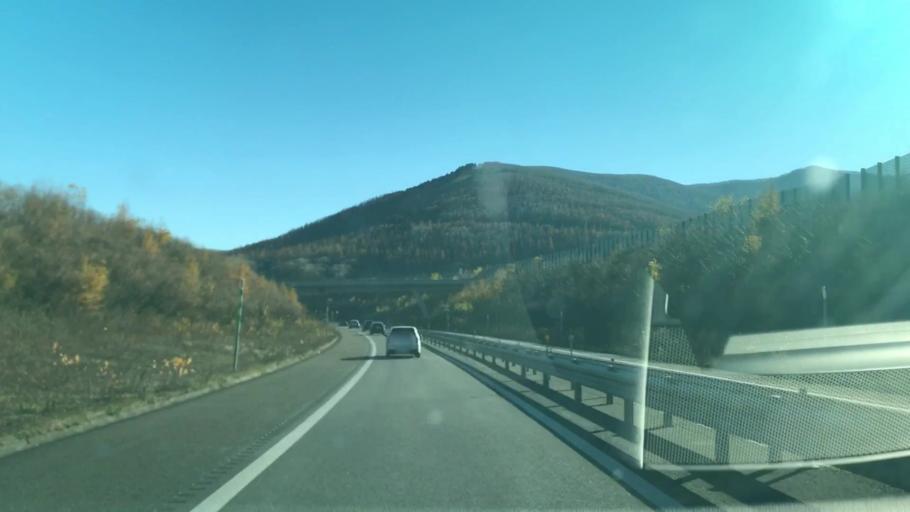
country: JP
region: Hokkaido
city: Otofuke
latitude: 43.0425
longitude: 142.7837
